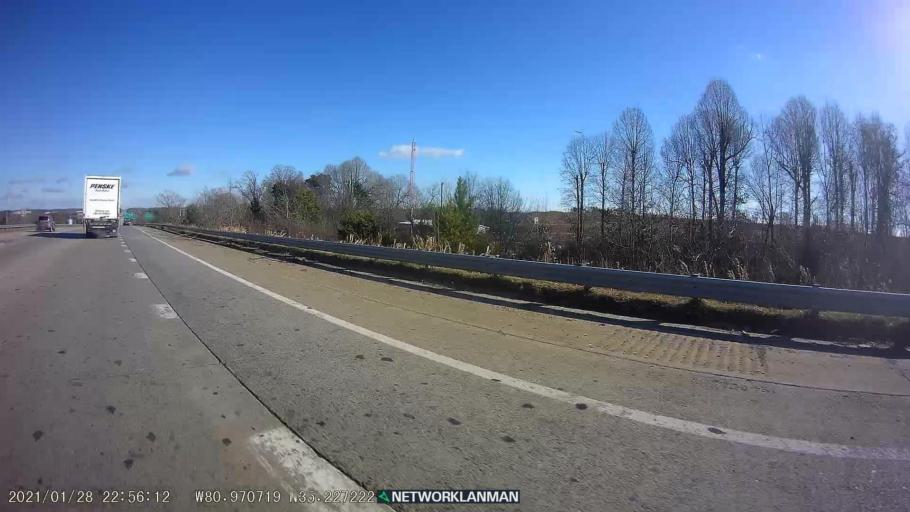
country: US
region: North Carolina
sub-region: Gaston County
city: Belmont
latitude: 35.2279
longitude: -80.9702
